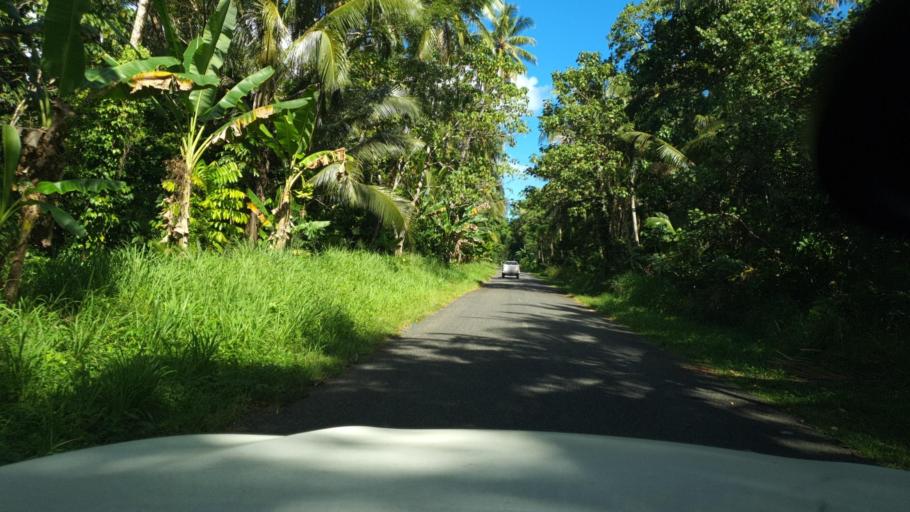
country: SB
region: Guadalcanal
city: Honiara
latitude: -9.2564
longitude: 159.6798
